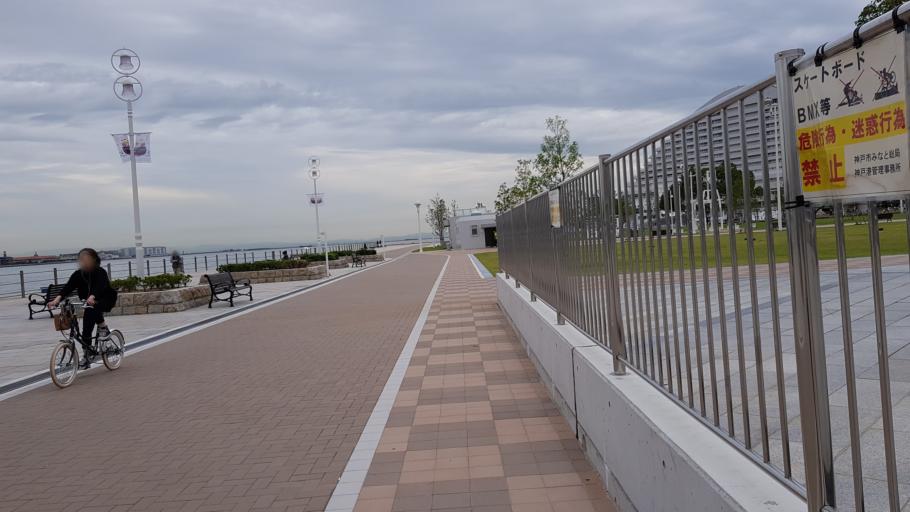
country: JP
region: Hyogo
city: Kobe
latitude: 34.6830
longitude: 135.1900
